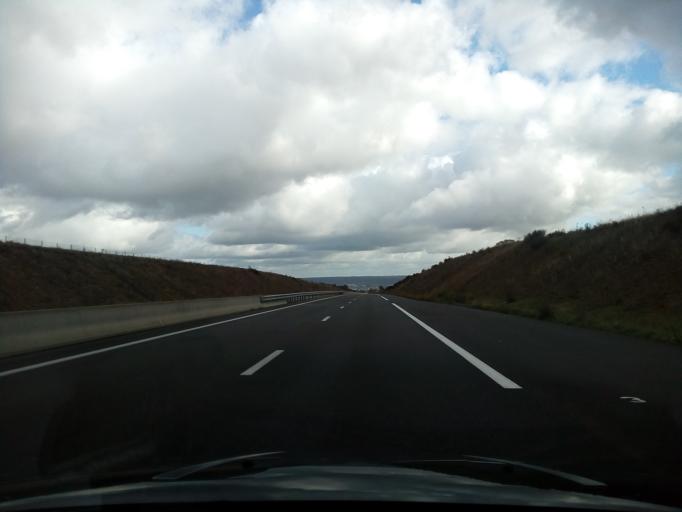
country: FR
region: Auvergne
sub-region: Departement de l'Allier
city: Quinssaines
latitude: 46.3179
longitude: 2.5039
